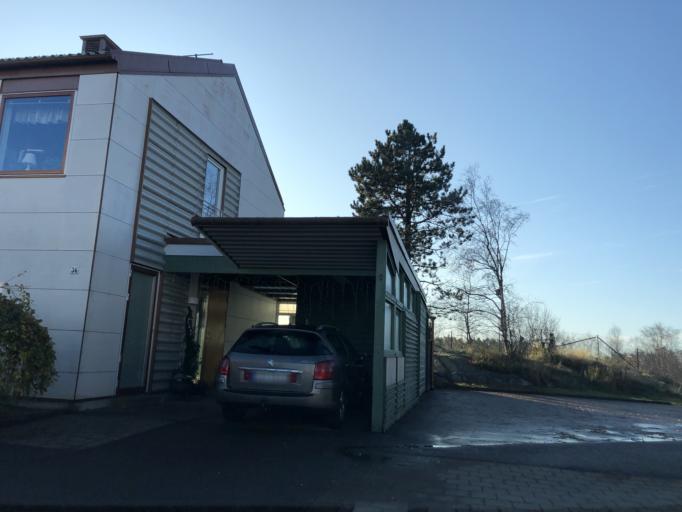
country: SE
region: Vaestra Goetaland
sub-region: Goteborg
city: Gardsten
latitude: 57.7993
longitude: 12.0311
